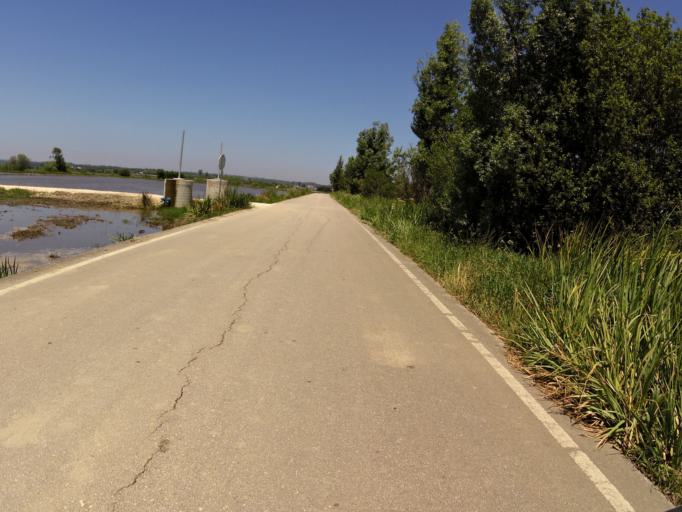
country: PT
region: Coimbra
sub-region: Montemor-O-Velho
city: Montemor-o-Velho
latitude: 40.1635
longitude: -8.7169
